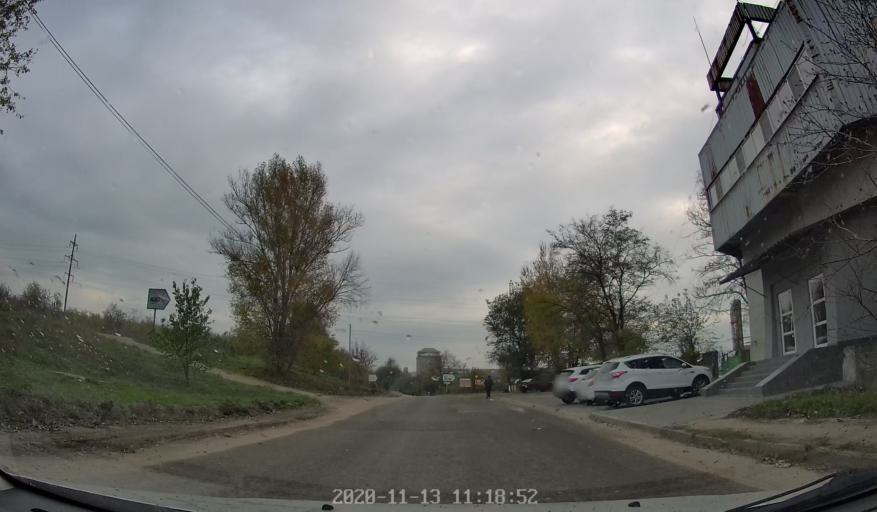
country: MD
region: Chisinau
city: Chisinau
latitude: 46.9896
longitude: 28.9146
